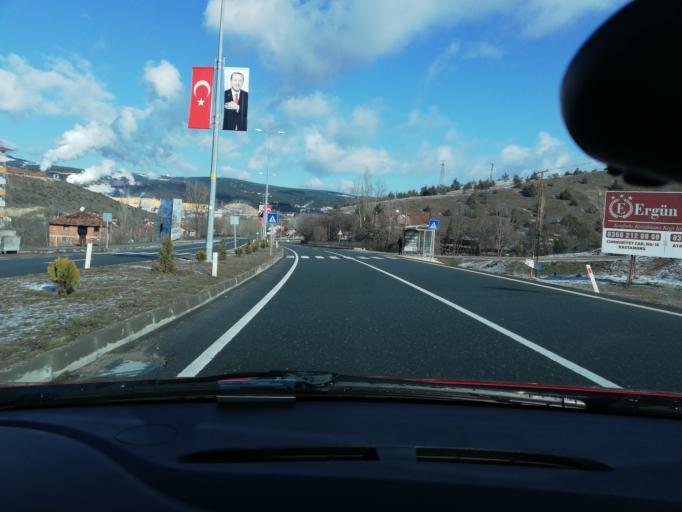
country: TR
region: Kastamonu
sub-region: Cide
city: Kastamonu
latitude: 41.3456
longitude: 33.7670
